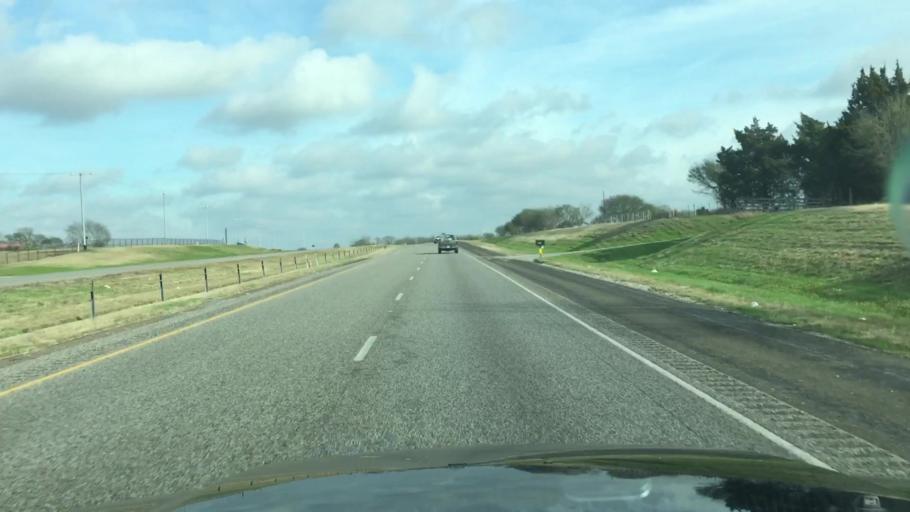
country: US
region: Texas
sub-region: Washington County
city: Brenham
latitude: 30.1364
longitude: -96.3397
